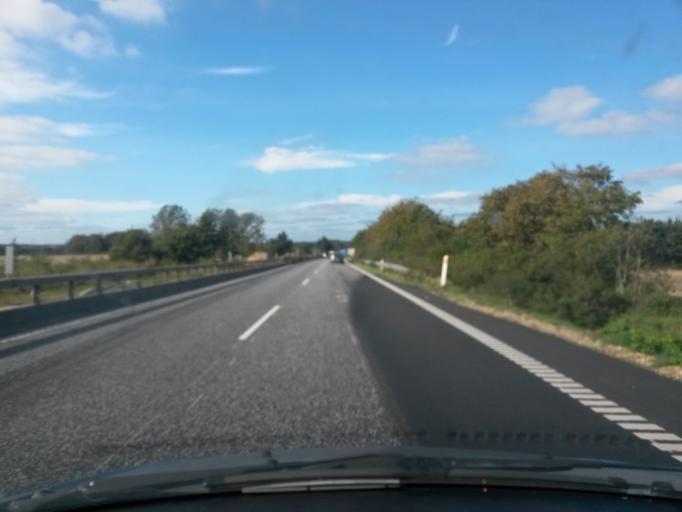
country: DK
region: Central Jutland
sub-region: Herning Kommune
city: Avlum
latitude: 56.2324
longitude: 8.8135
